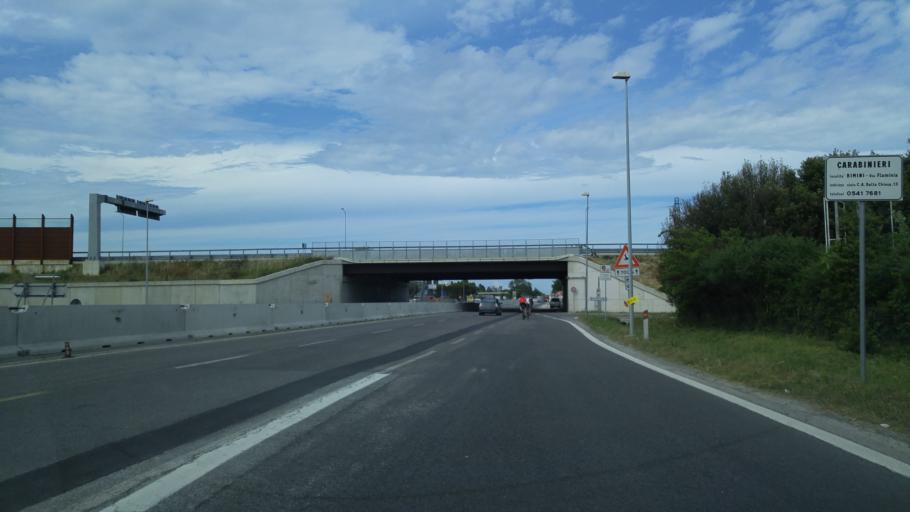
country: IT
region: Emilia-Romagna
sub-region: Provincia di Rimini
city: Rimini
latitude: 44.0373
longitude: 12.5648
